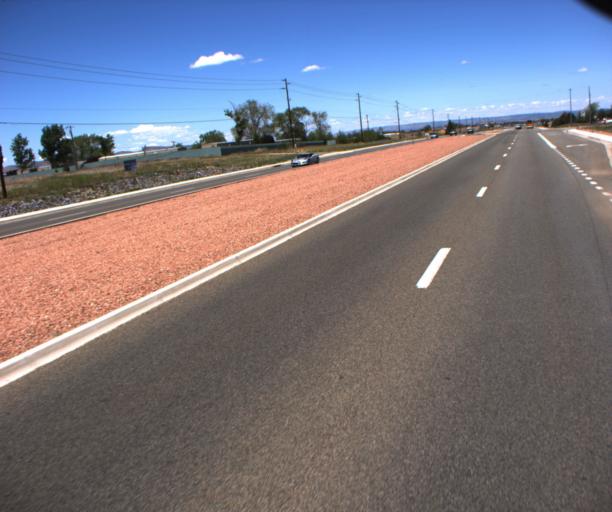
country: US
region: Arizona
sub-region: Yavapai County
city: Chino Valley
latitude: 34.7192
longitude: -112.4534
